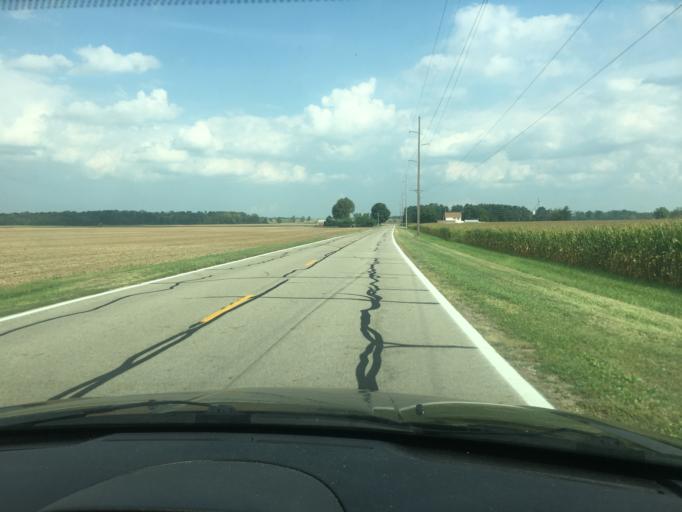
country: US
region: Ohio
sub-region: Champaign County
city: Urbana
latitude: 40.1297
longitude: -83.8050
